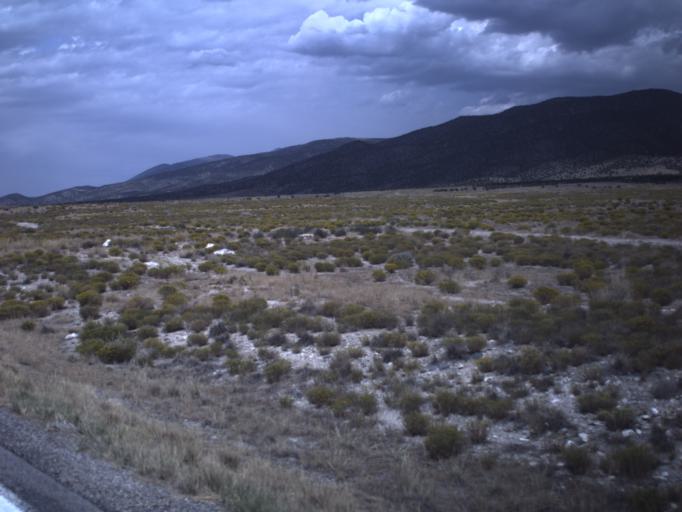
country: US
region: Utah
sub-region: Utah County
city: Eagle Mountain
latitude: 40.2569
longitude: -112.2263
